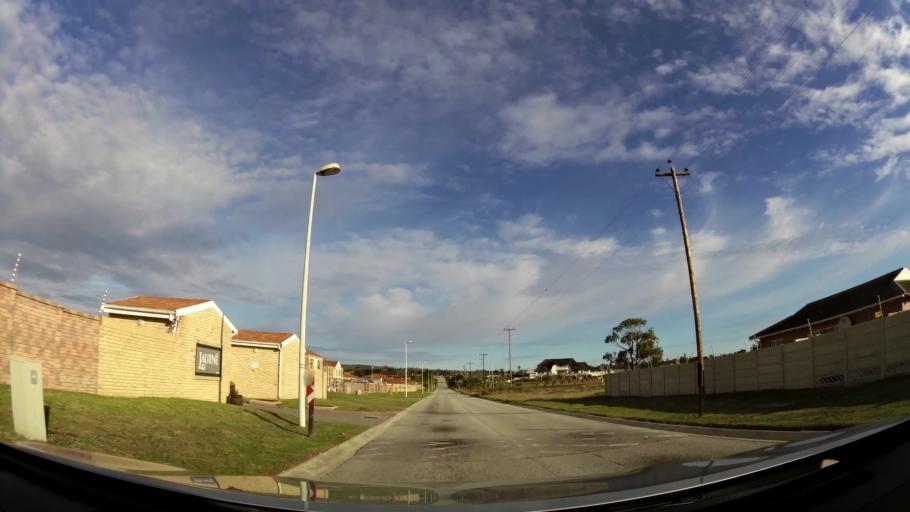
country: ZA
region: Eastern Cape
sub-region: Nelson Mandela Bay Metropolitan Municipality
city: Port Elizabeth
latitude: -33.9527
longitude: 25.4875
